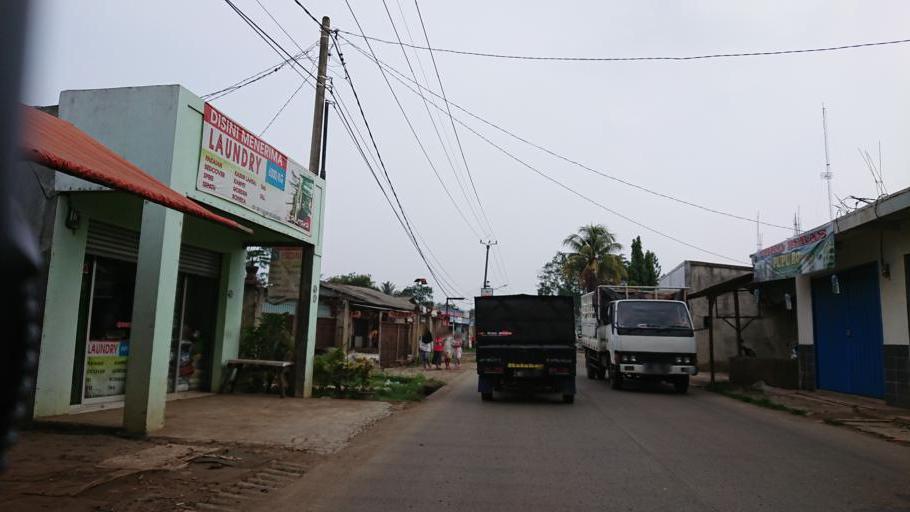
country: ID
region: West Java
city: Parung
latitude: -6.3974
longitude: 106.6874
